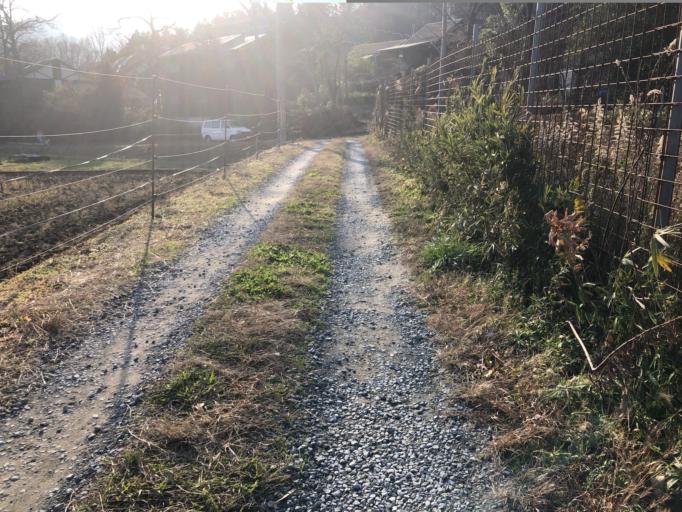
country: JP
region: Kyoto
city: Kameoka
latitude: 35.0577
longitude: 135.4764
